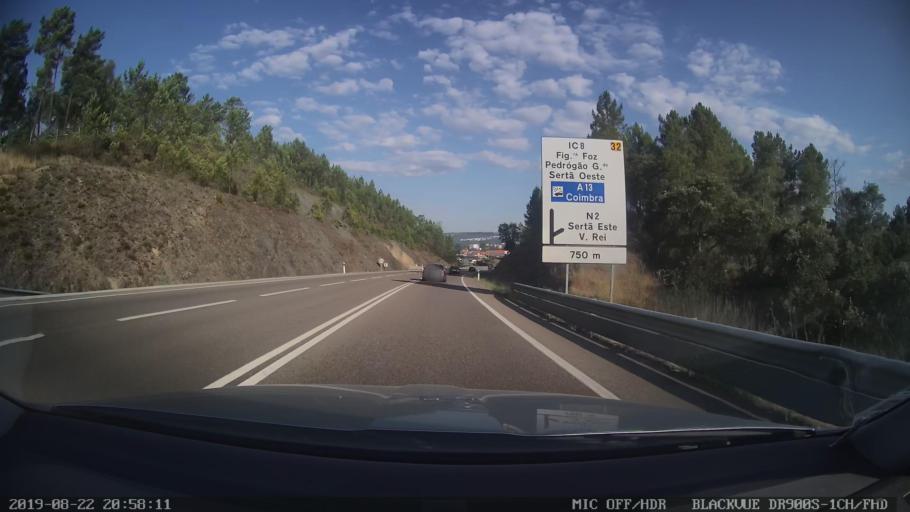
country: PT
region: Castelo Branco
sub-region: Serta
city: Serta
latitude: 39.7981
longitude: -8.0780
